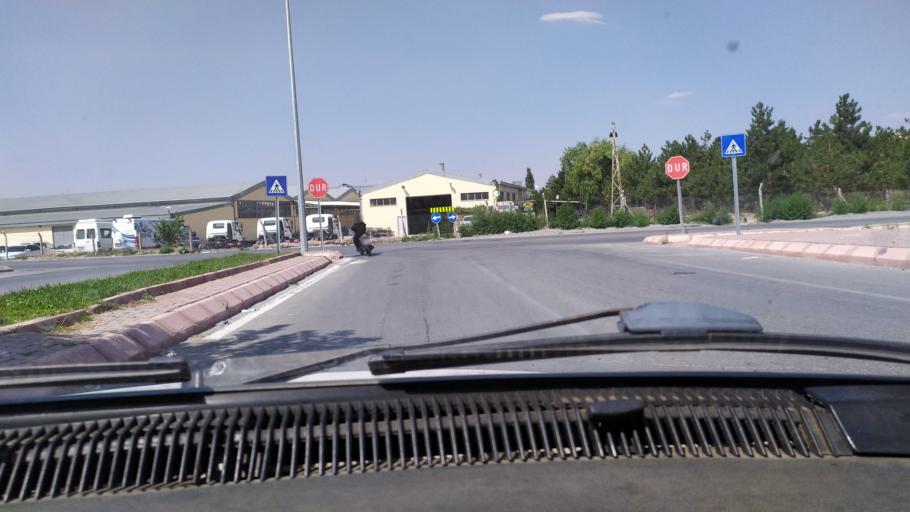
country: TR
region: Kayseri
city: Talas
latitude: 38.7193
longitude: 35.5551
